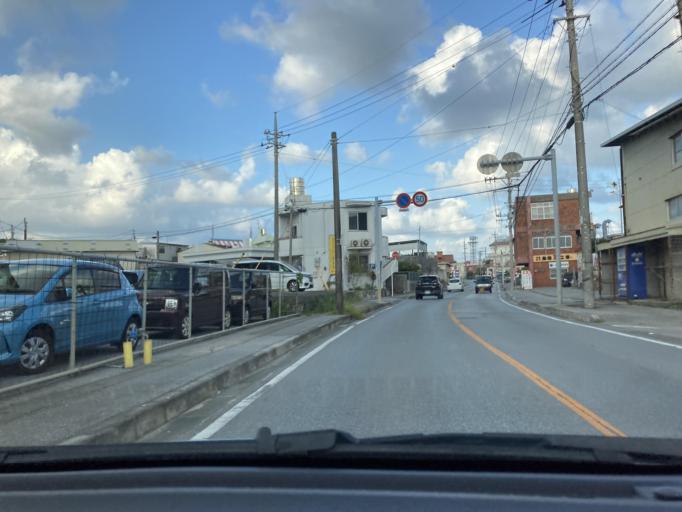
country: JP
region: Okinawa
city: Ginowan
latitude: 26.1980
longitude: 127.7481
